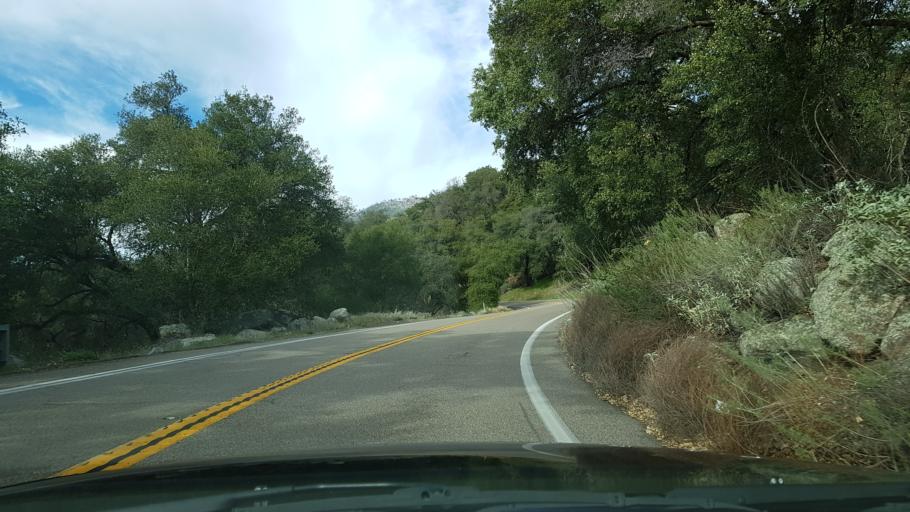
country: US
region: California
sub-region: Riverside County
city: Aguanga
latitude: 33.2942
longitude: -116.8902
